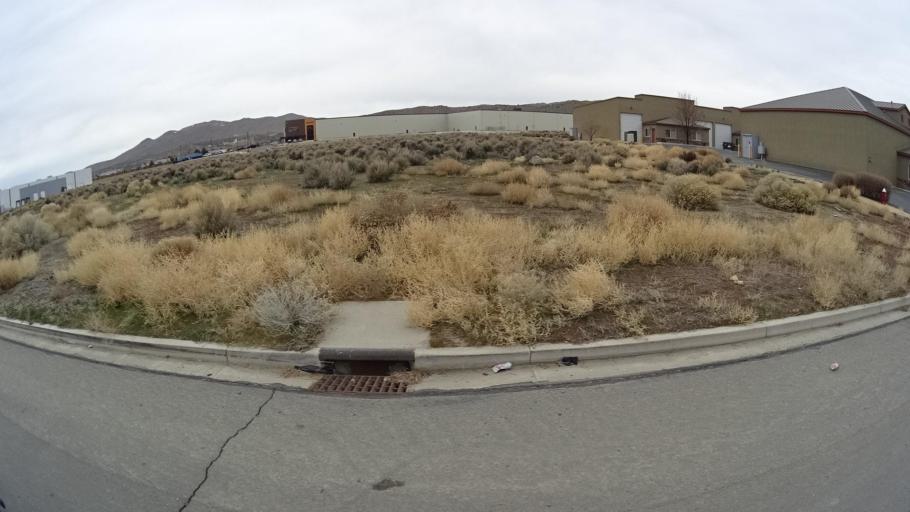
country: US
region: Nevada
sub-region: Washoe County
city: Spanish Springs
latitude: 39.6757
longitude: -119.7152
